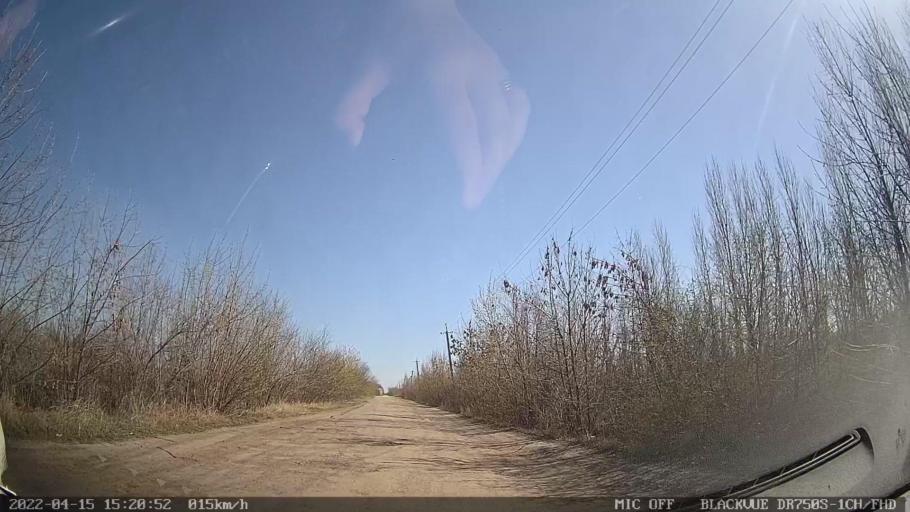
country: MD
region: Raionul Ocnita
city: Otaci
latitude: 48.3850
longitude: 27.9091
